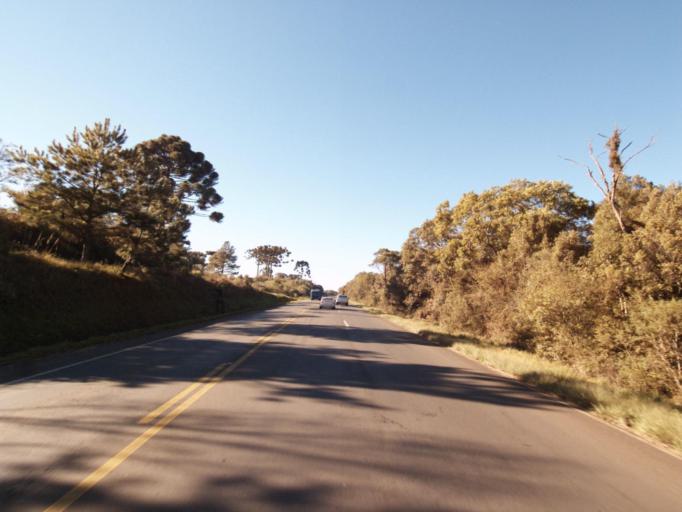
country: BR
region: Santa Catarina
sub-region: Concordia
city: Concordia
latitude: -26.9111
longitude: -51.9650
